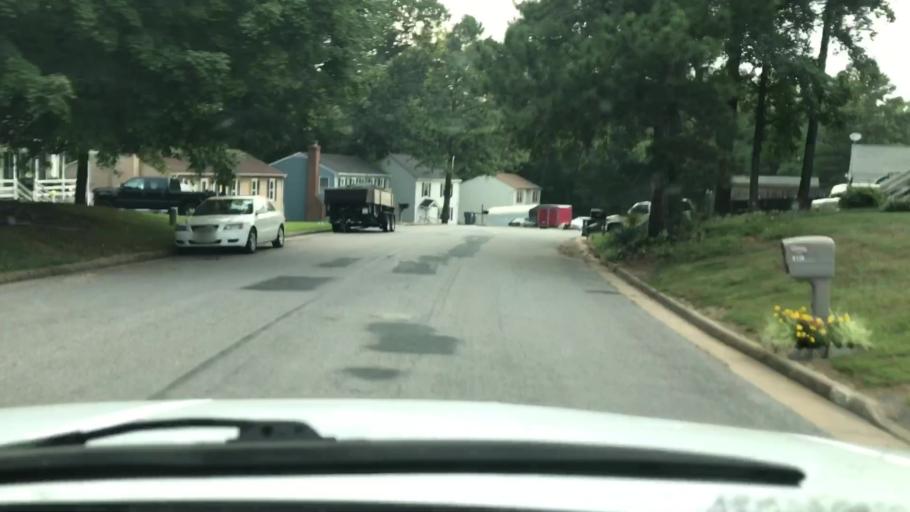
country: US
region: Virginia
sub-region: Chesterfield County
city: Chesterfield
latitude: 37.4413
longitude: -77.5186
